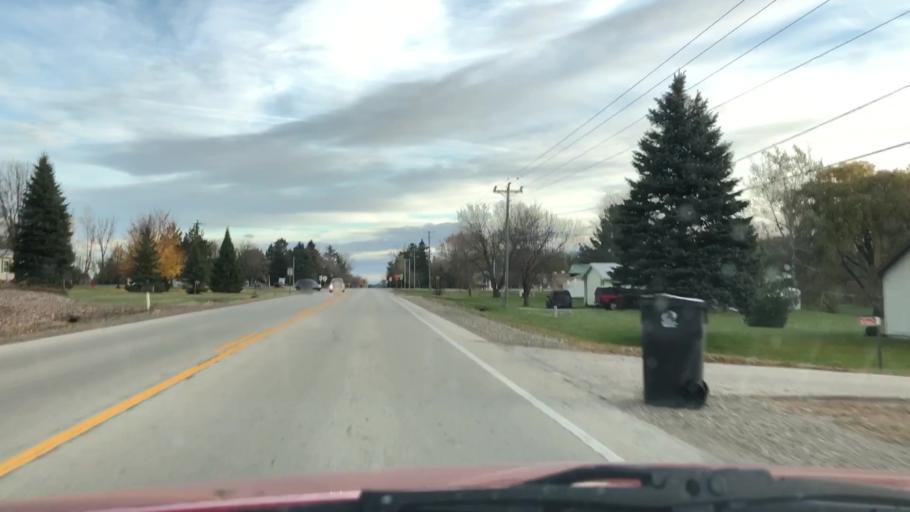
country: US
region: Wisconsin
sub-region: Brown County
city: Oneida
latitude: 44.4431
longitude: -88.2280
